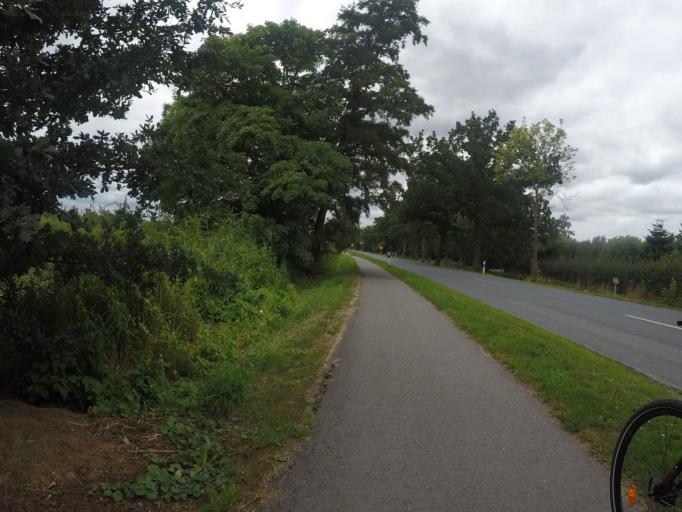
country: DE
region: Lower Saxony
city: Grossenworden
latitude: 53.6771
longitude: 9.2711
